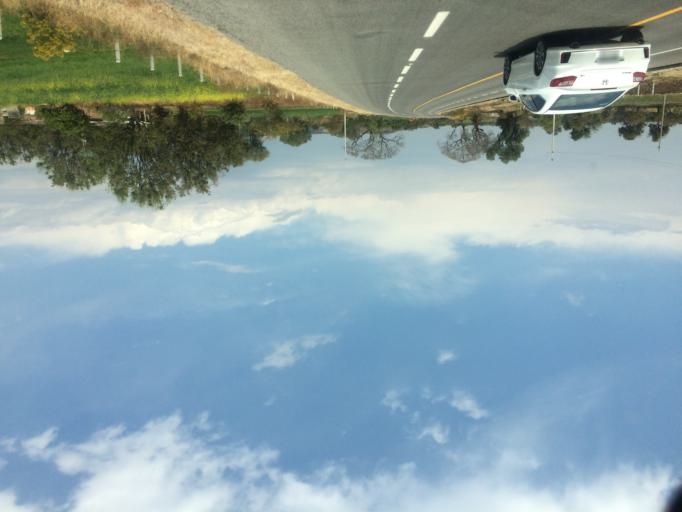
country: MX
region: Guanajuato
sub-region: Silao de la Victoria
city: Loma de Yerbabuena
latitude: 21.0266
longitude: -101.4463
